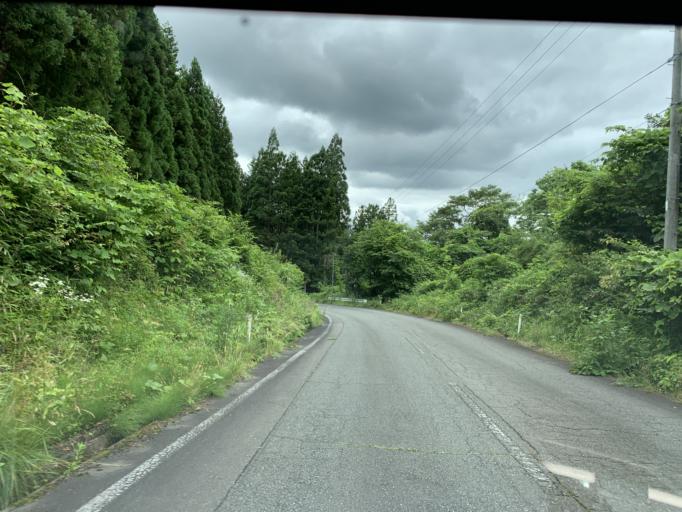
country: JP
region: Iwate
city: Ichinoseki
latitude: 38.8918
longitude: 140.9816
